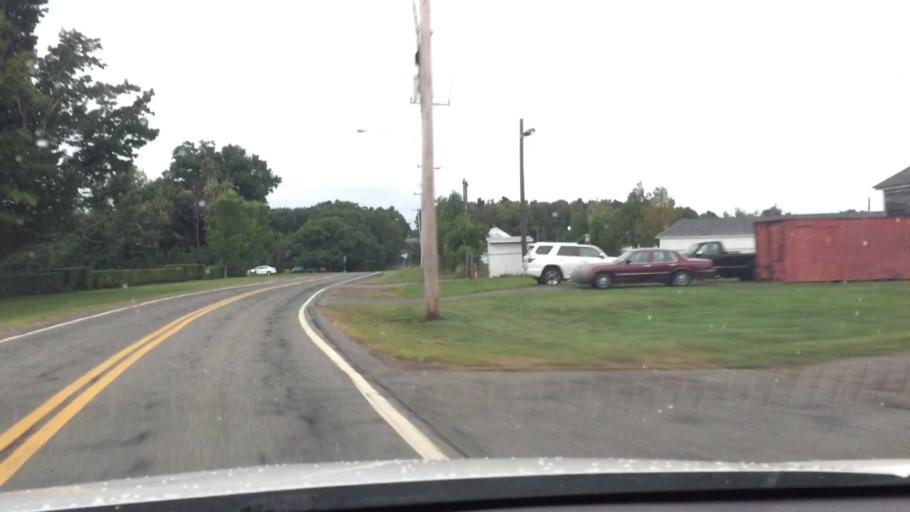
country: US
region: Massachusetts
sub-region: Hampden County
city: Granville
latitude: 42.1821
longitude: -72.9293
